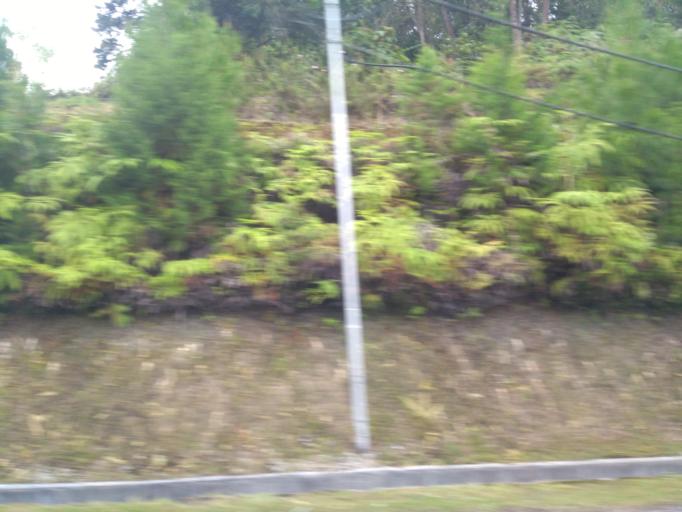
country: MY
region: Pahang
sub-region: Cameron Highlands
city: Tanah Rata
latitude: 4.4835
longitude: 101.3785
